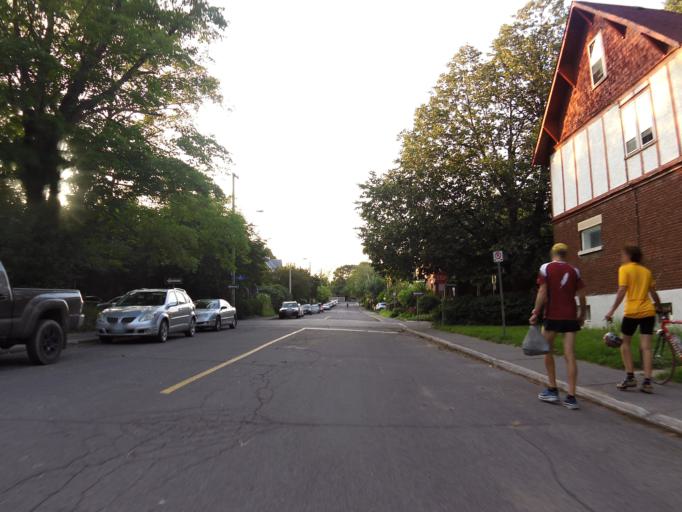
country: CA
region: Ontario
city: Ottawa
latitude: 45.3917
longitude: -75.6847
